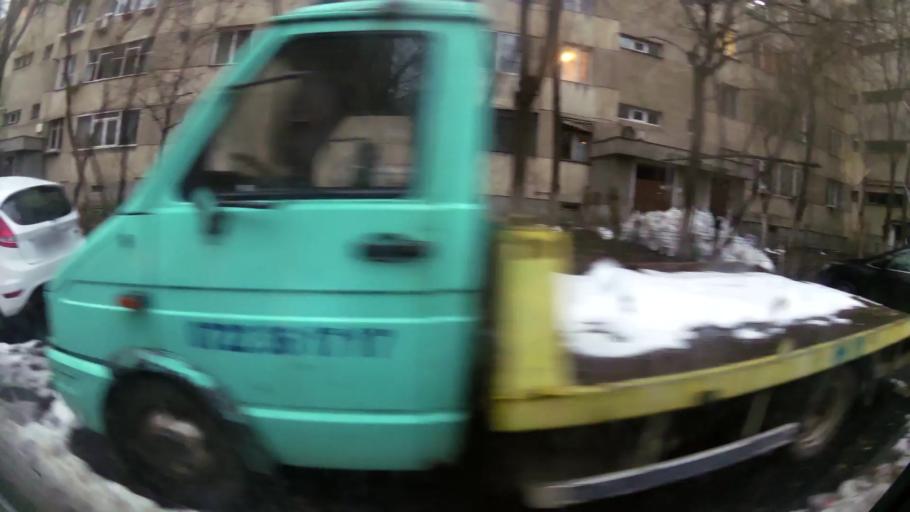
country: RO
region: Ilfov
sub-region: Comuna Chiajna
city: Rosu
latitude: 44.4337
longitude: 26.0296
